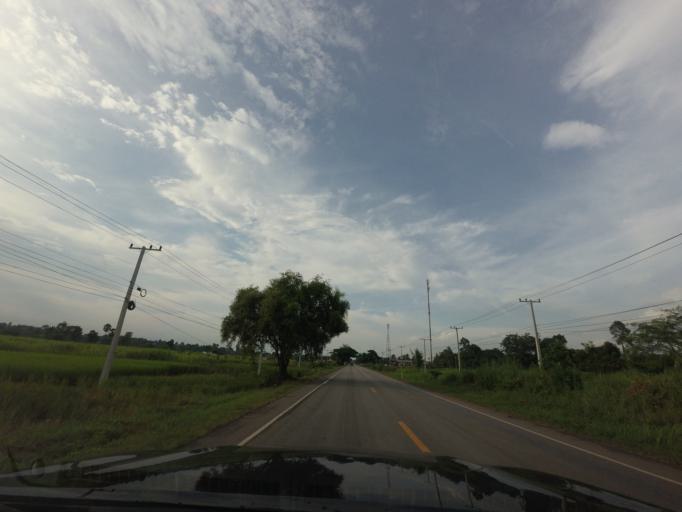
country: TH
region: Nong Khai
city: Pho Tak
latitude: 17.7655
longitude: 102.3971
